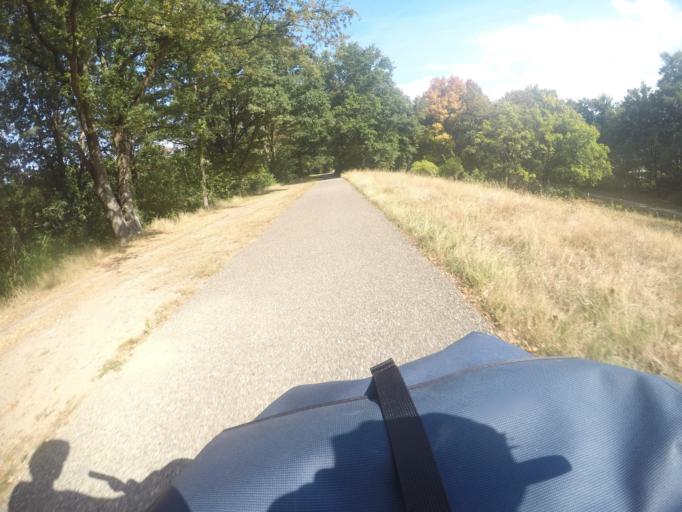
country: NL
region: Gelderland
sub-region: Gemeente Renkum
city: Oosterbeek
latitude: 51.9887
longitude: 5.8555
